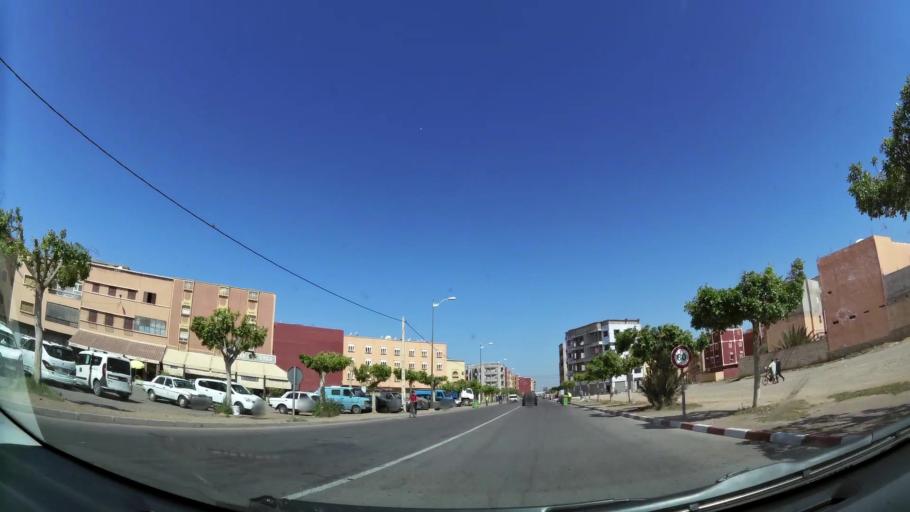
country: MA
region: Souss-Massa-Draa
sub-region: Inezgane-Ait Mellou
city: Inezgane
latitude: 30.3380
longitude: -9.5043
